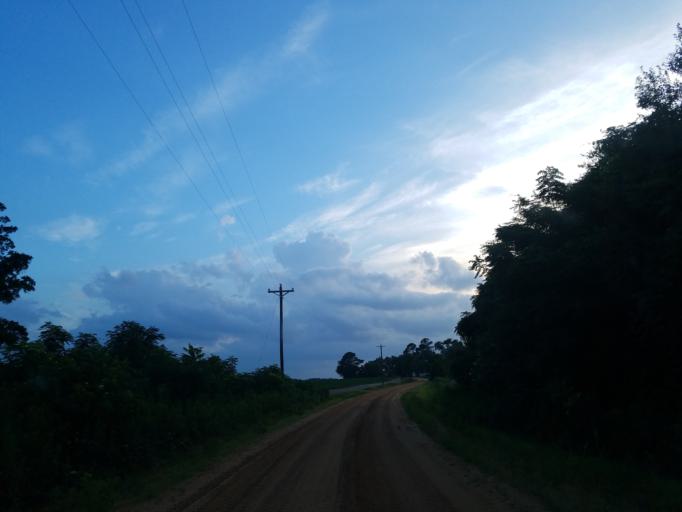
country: US
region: Georgia
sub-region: Dooly County
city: Vienna
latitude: 32.1460
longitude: -83.7352
